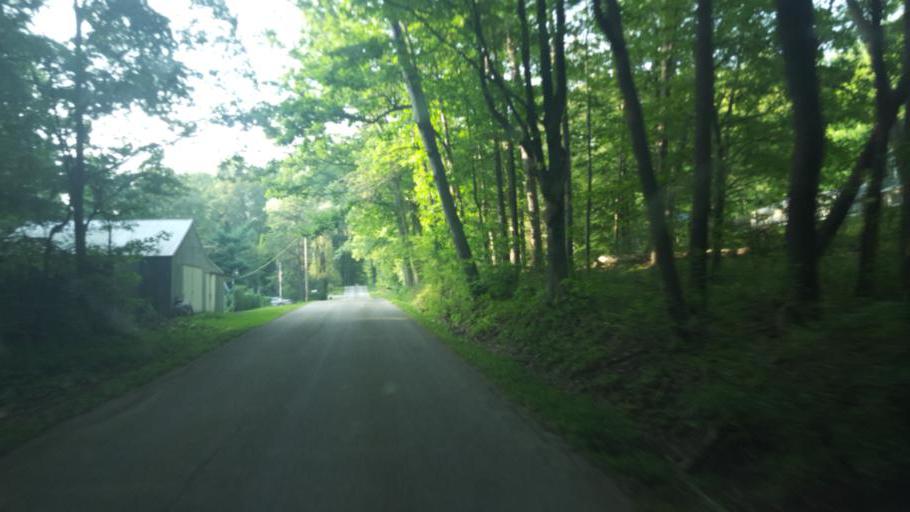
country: US
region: Ohio
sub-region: Sandusky County
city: Bellville
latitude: 40.6346
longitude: -82.4849
